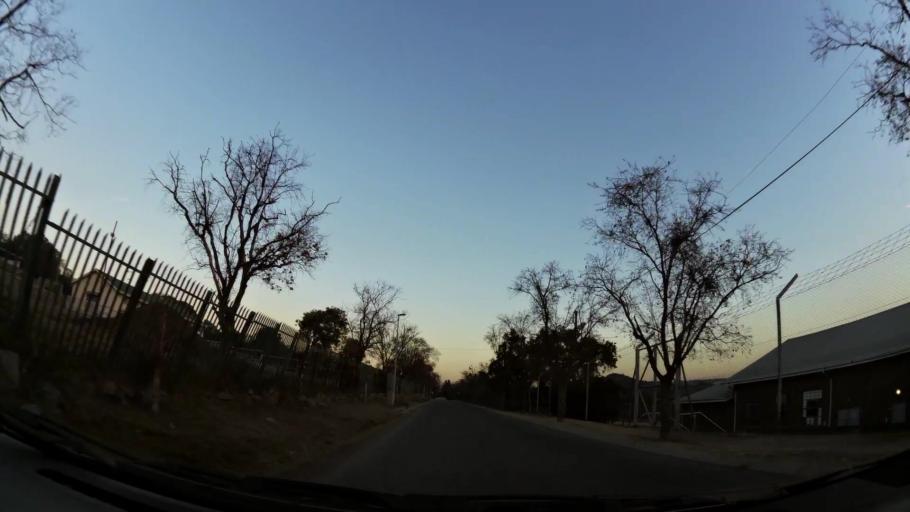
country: ZA
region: Gauteng
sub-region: City of Johannesburg Metropolitan Municipality
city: Midrand
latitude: -26.0072
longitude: 28.0524
